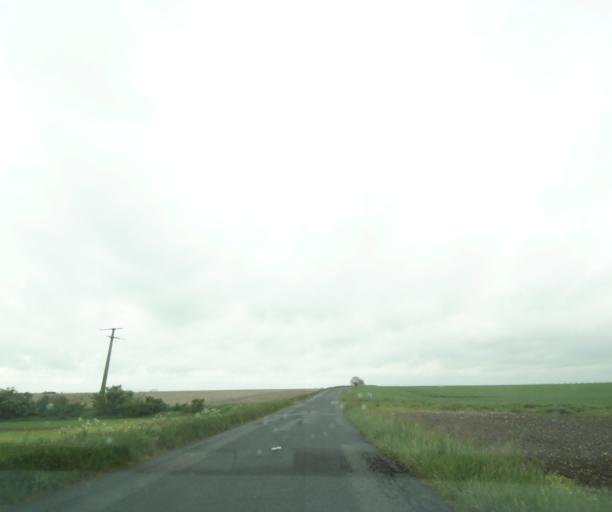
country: FR
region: Poitou-Charentes
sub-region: Departement de la Charente-Maritime
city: Pons
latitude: 45.6427
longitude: -0.5677
